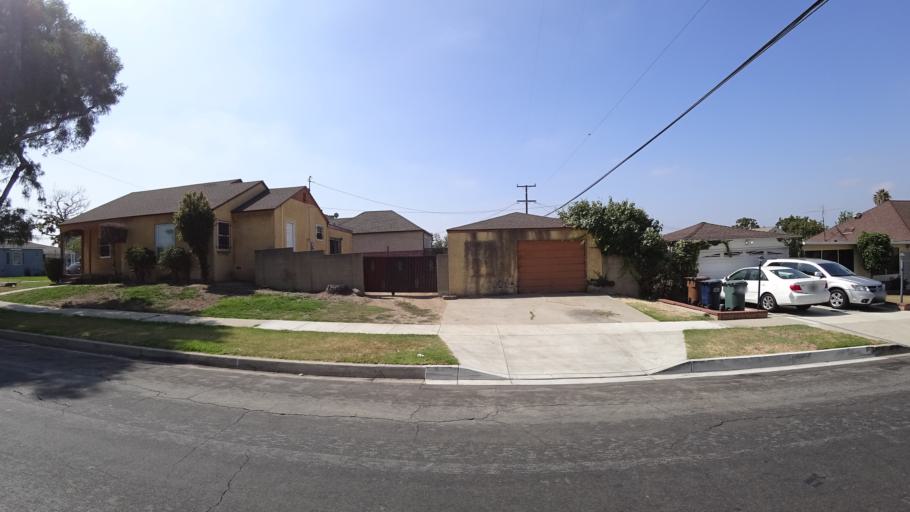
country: US
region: California
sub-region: Los Angeles County
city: Westmont
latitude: 33.9418
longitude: -118.3138
